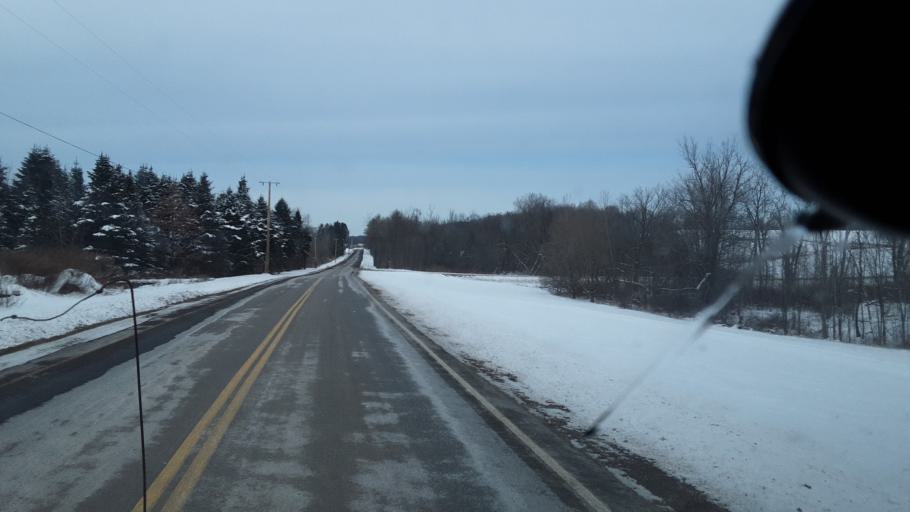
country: US
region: New York
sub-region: Wayne County
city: Lyons
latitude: 43.0984
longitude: -77.0433
